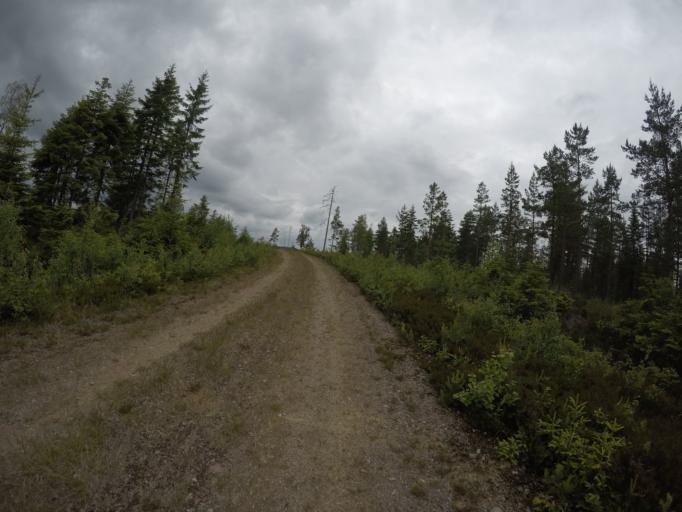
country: SE
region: Dalarna
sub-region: Ludvika Kommun
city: Abborrberget
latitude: 60.0876
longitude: 14.5090
